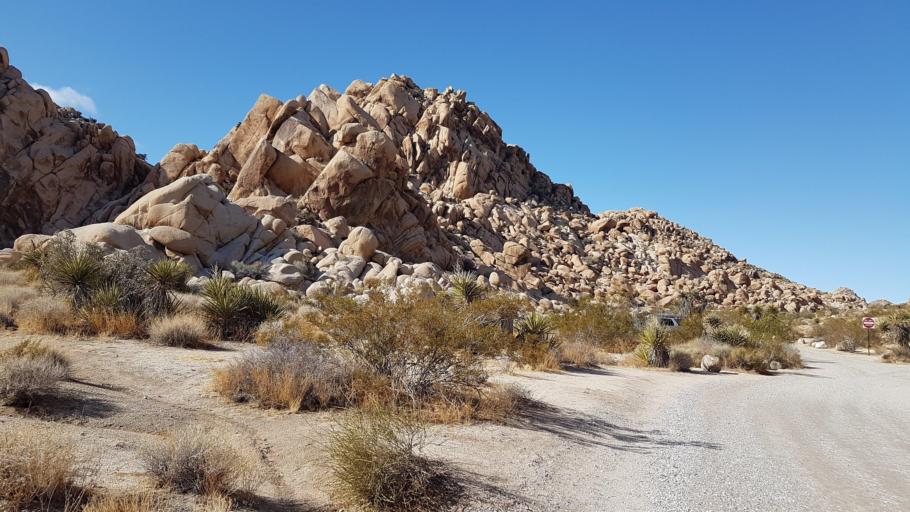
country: US
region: California
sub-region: San Bernardino County
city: Twentynine Palms
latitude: 34.0928
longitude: -116.1631
